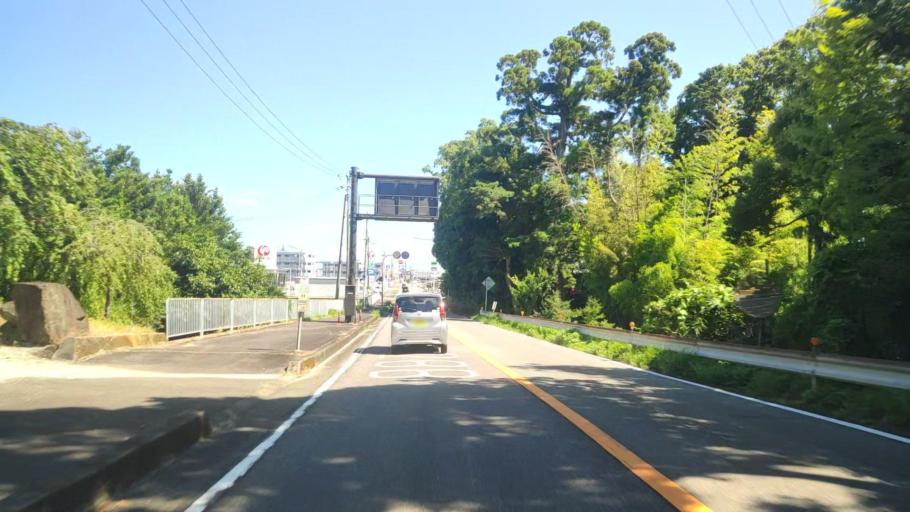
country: JP
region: Wakayama
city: Shingu
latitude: 33.5852
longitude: 135.9186
